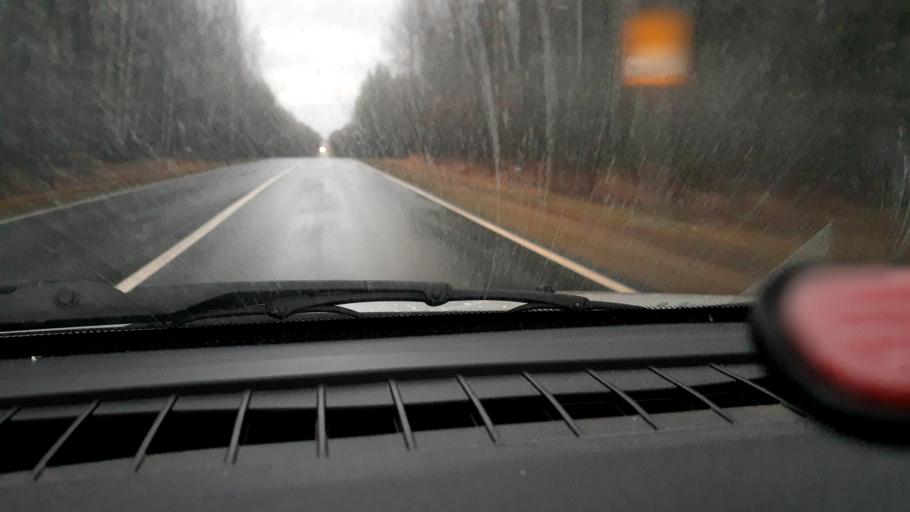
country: RU
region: Nizjnij Novgorod
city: Uren'
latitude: 57.2632
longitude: 45.6181
